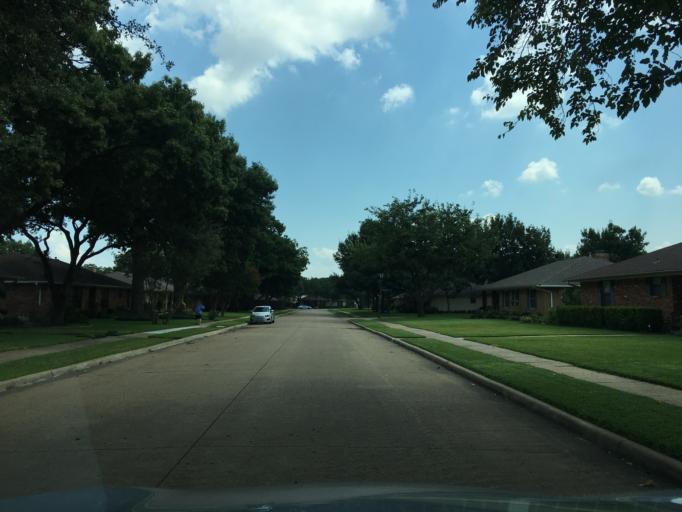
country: US
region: Texas
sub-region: Dallas County
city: Garland
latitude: 32.9373
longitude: -96.6462
